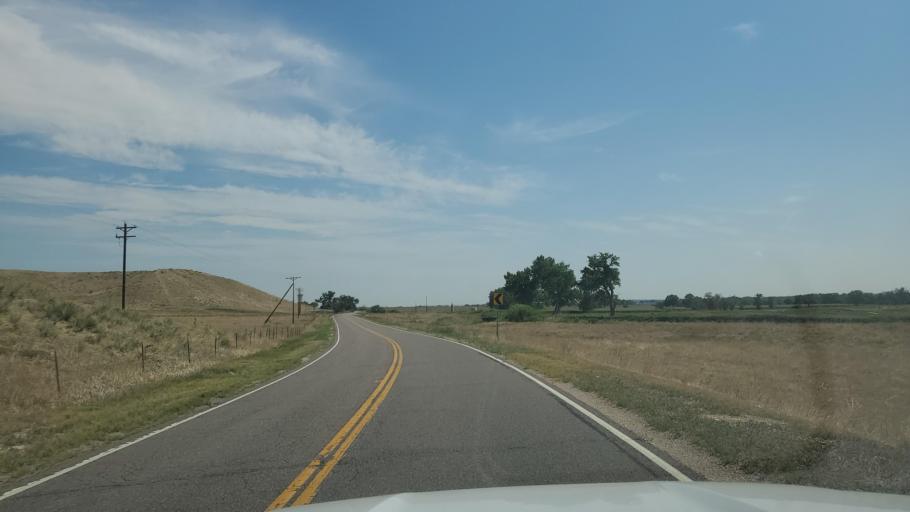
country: US
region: Colorado
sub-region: Adams County
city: Todd Creek
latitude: 39.9406
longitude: -104.8734
